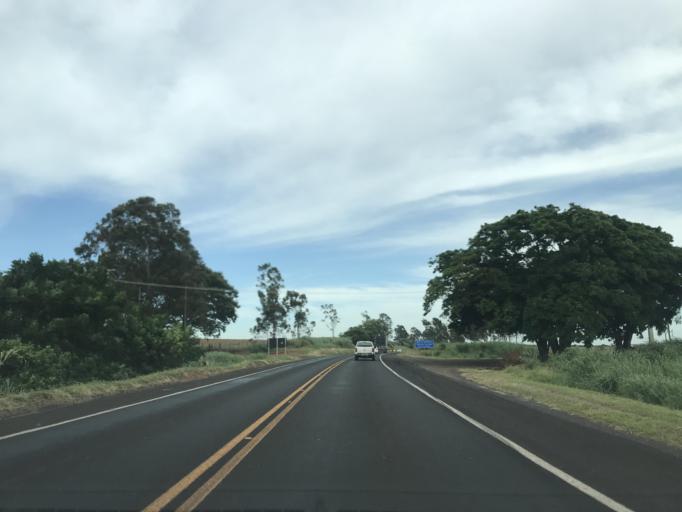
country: BR
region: Parana
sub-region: Paranavai
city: Paranavai
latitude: -23.0150
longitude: -52.5307
